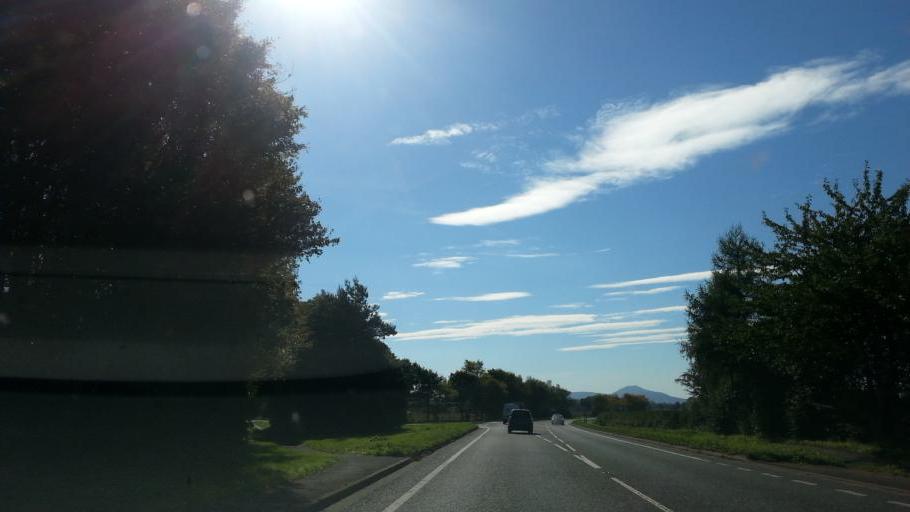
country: GB
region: England
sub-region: Telford and Wrekin
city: Chetwynd
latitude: 52.7386
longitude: -2.4084
